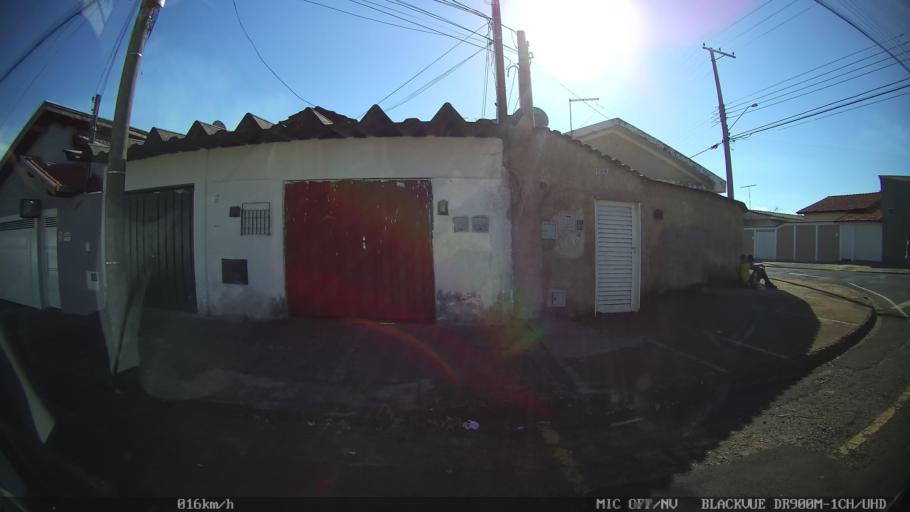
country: BR
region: Sao Paulo
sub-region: Franca
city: Franca
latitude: -20.5028
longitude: -47.4178
